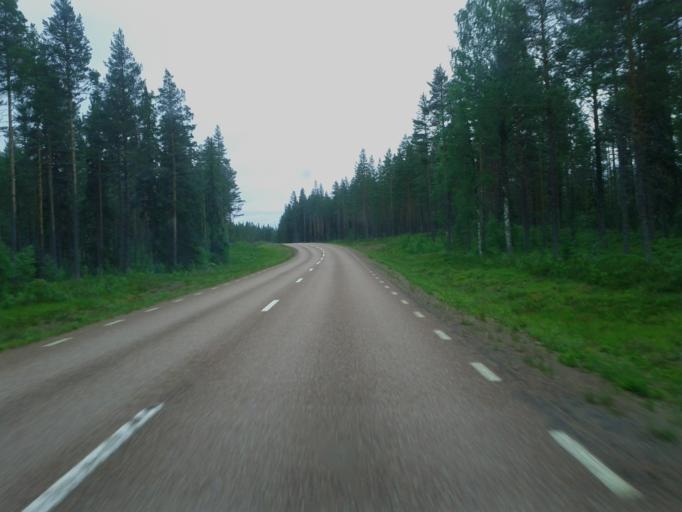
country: SE
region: Dalarna
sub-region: Alvdalens Kommun
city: AElvdalen
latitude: 61.4913
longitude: 13.4183
